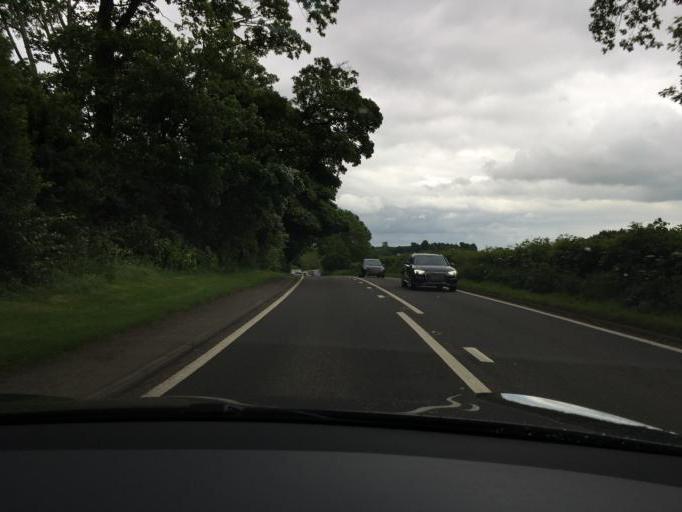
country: GB
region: England
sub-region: Derbyshire
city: Shirley
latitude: 52.9927
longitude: -1.6912
